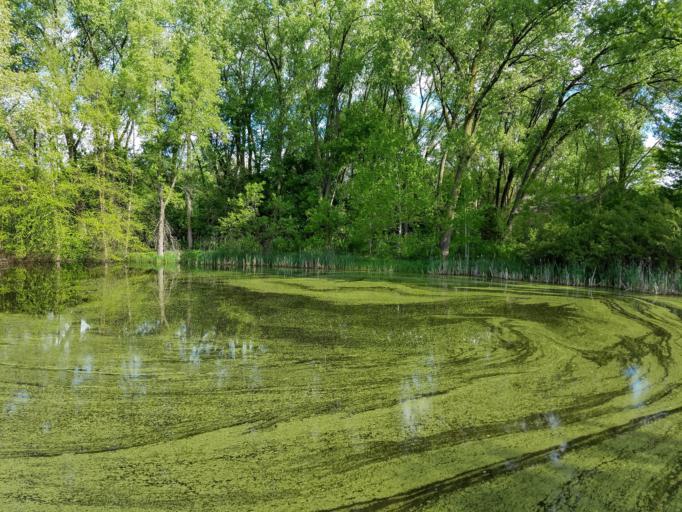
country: US
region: Wisconsin
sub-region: Dane County
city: Monona
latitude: 43.0546
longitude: -89.3161
